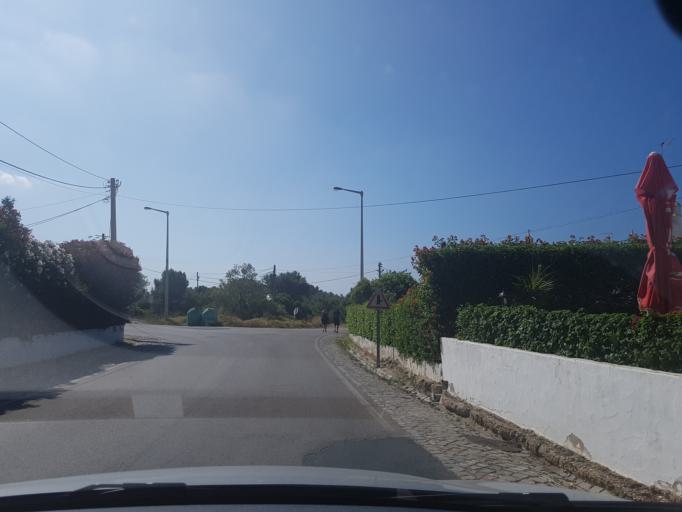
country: PT
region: Faro
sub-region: Lagoa
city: Carvoeiro
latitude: 37.0918
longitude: -8.4443
